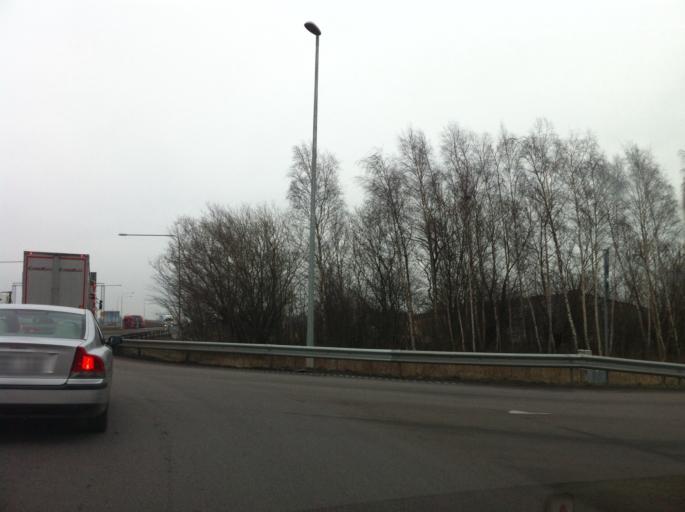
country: SE
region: Skane
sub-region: Landskrona
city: Landskrona
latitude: 55.8737
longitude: 12.8680
